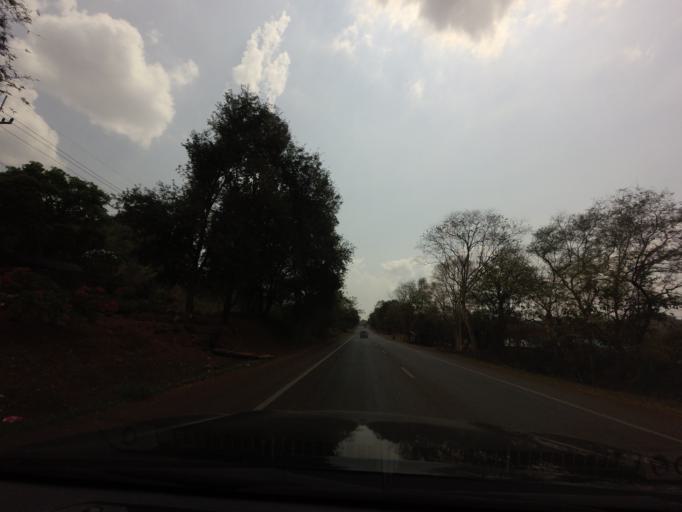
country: TH
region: Kanchanaburi
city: Sai Yok
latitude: 14.1459
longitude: 99.1455
